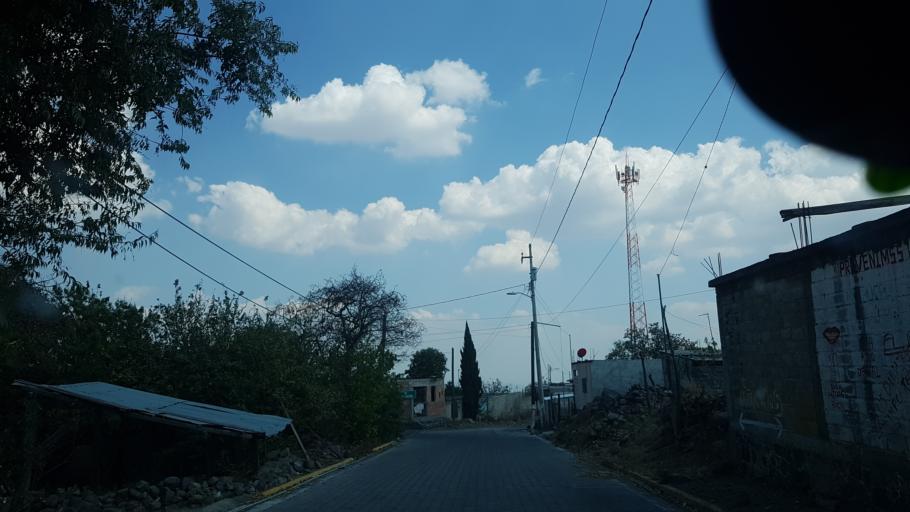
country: MX
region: Puebla
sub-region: Atlixco
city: San Pedro Benito Juarez
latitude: 18.9481
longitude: -98.5485
